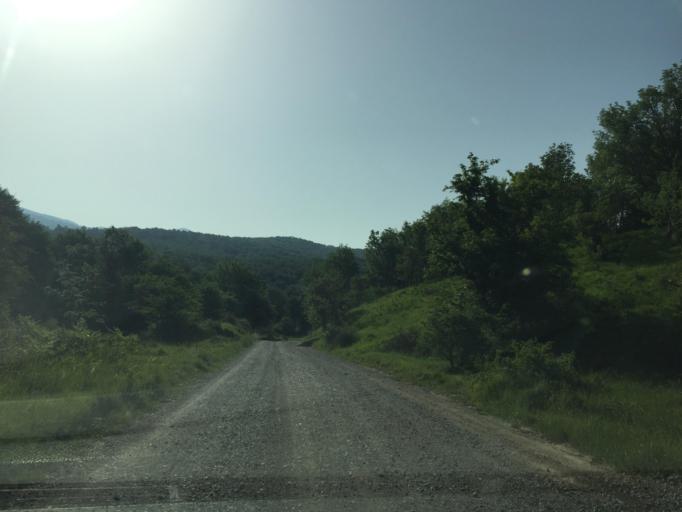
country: HR
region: Primorsko-Goranska
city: Klana
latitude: 45.4690
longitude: 14.4049
